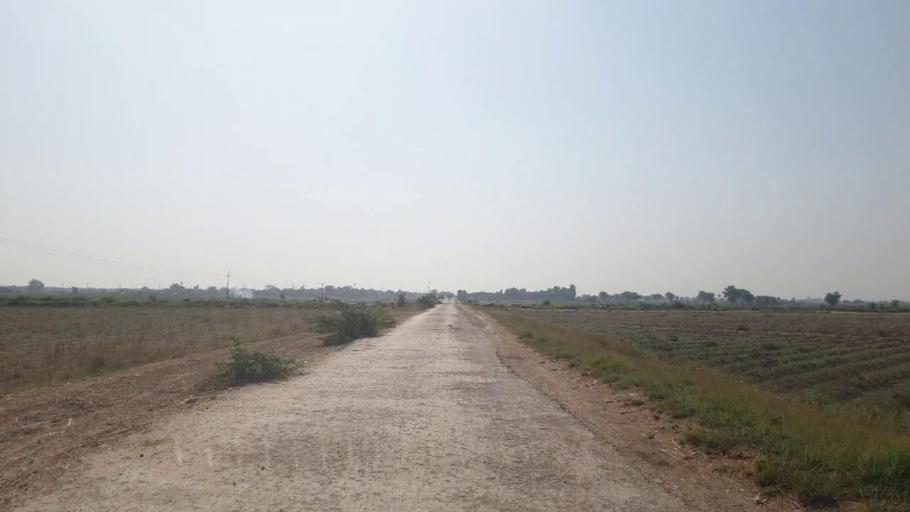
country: PK
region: Sindh
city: Berani
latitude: 25.8995
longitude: 68.7473
